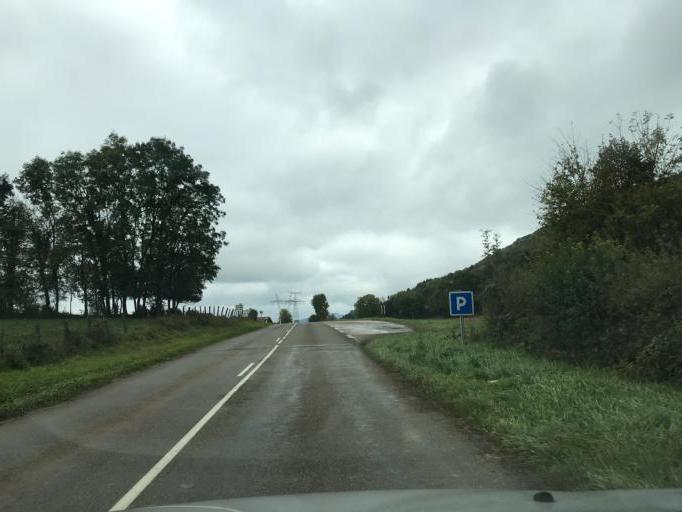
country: FR
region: Bourgogne
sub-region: Departement de Saone-et-Loire
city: Cuiseaux
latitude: 46.4244
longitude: 5.4556
